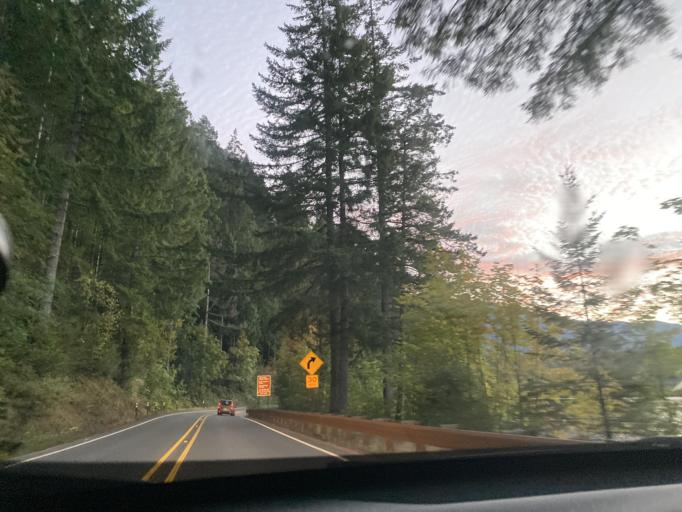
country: CA
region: British Columbia
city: Sooke
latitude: 48.0609
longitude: -123.7790
